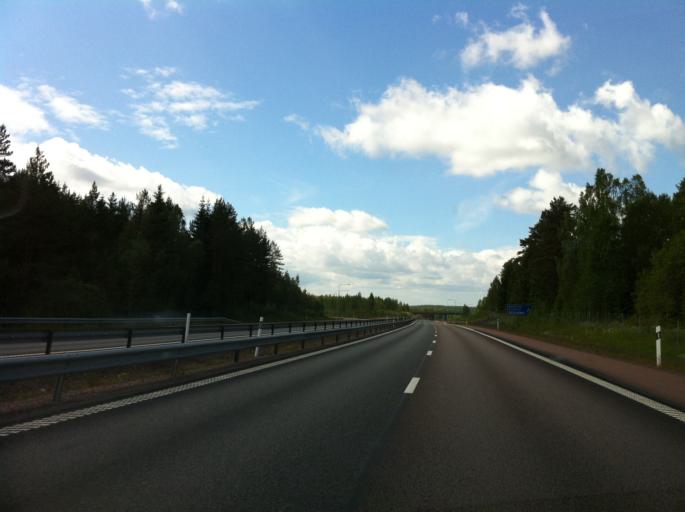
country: SE
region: Vaermland
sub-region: Grums Kommun
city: Slottsbron
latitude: 59.2881
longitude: 13.0501
